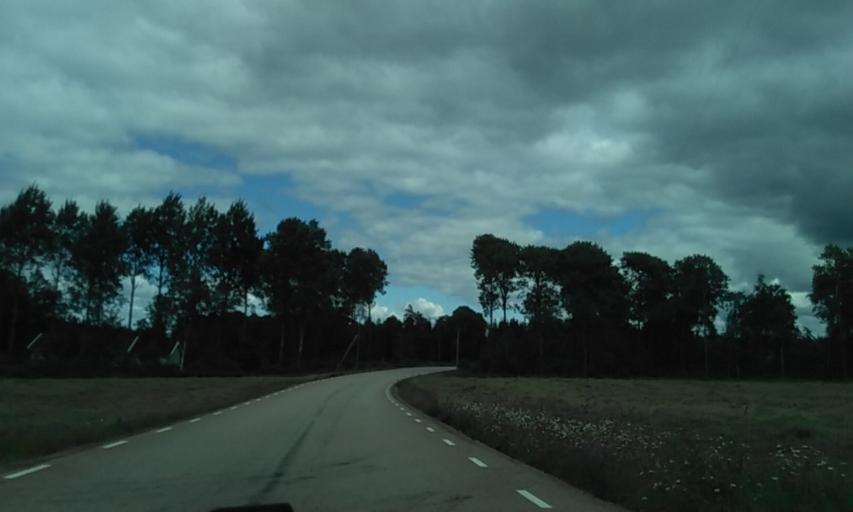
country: SE
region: Vaestra Goetaland
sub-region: Boras Kommun
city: Sjomarken
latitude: 57.7951
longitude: 12.8769
